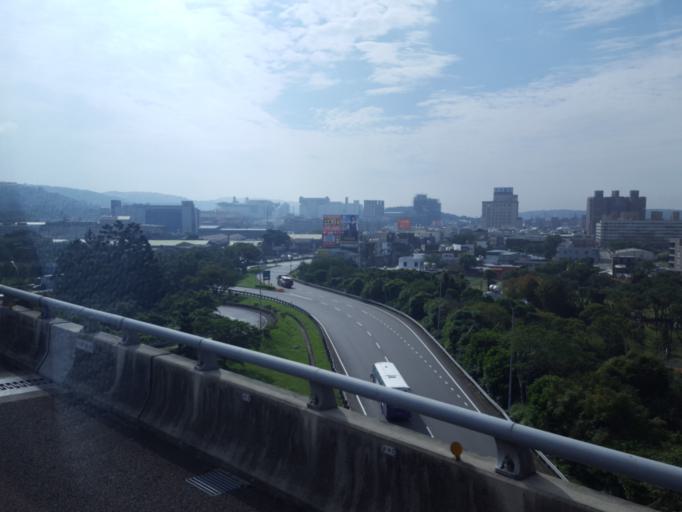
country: TW
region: Taiwan
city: Daxi
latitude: 24.9111
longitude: 121.1649
